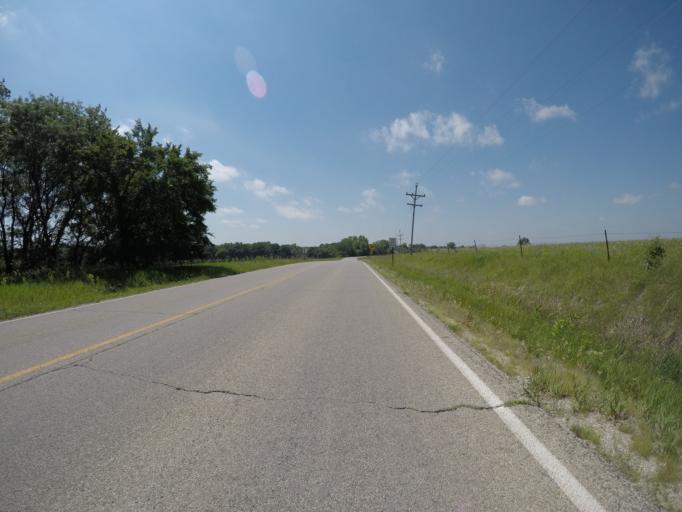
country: US
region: Kansas
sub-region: Pottawatomie County
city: Westmoreland
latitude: 39.3673
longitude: -96.4268
